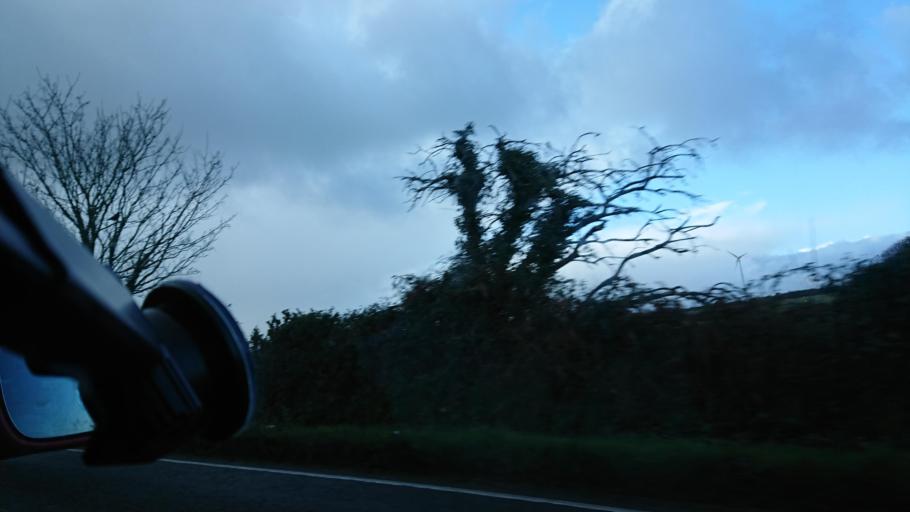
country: GB
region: England
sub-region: Cornwall
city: Looe
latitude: 50.3518
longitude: -4.4750
